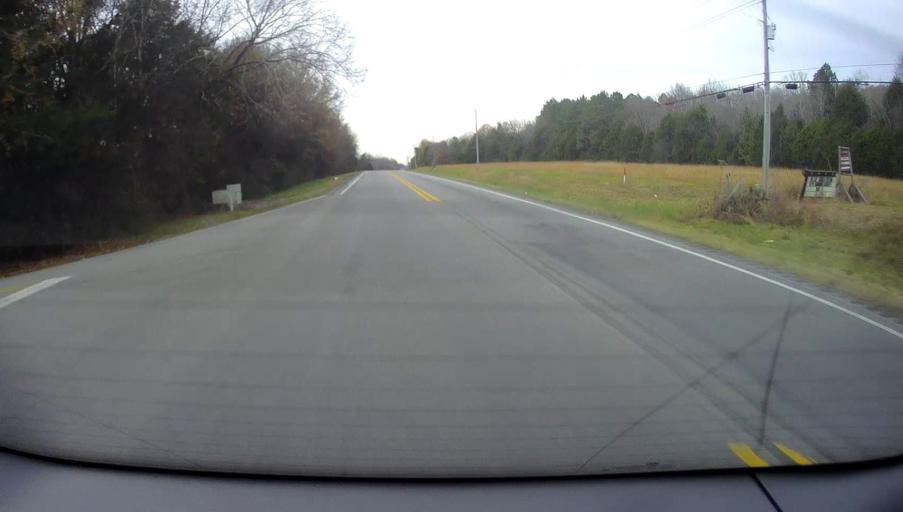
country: US
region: Alabama
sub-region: Morgan County
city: Priceville
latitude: 34.4353
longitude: -86.7389
